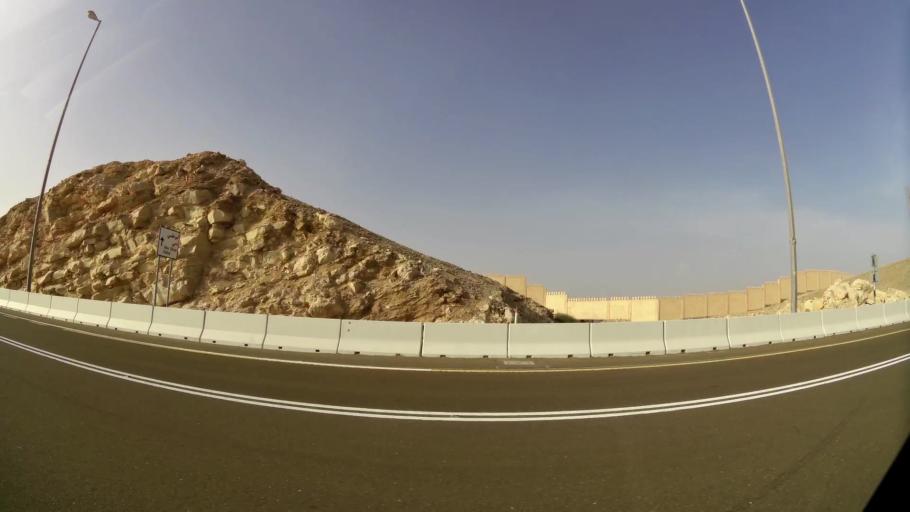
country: AE
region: Abu Dhabi
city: Al Ain
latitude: 24.1111
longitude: 55.7562
